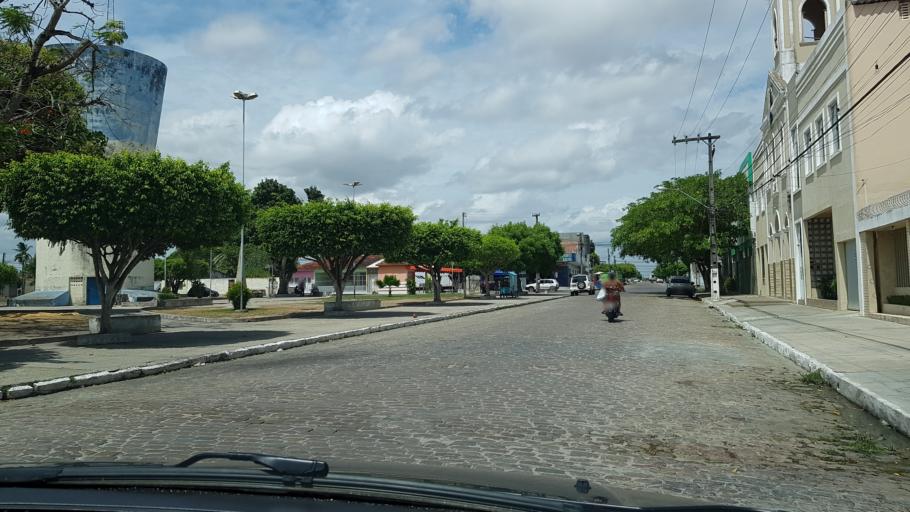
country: BR
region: Alagoas
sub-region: Penedo
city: Penedo
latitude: -10.2802
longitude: -36.5630
